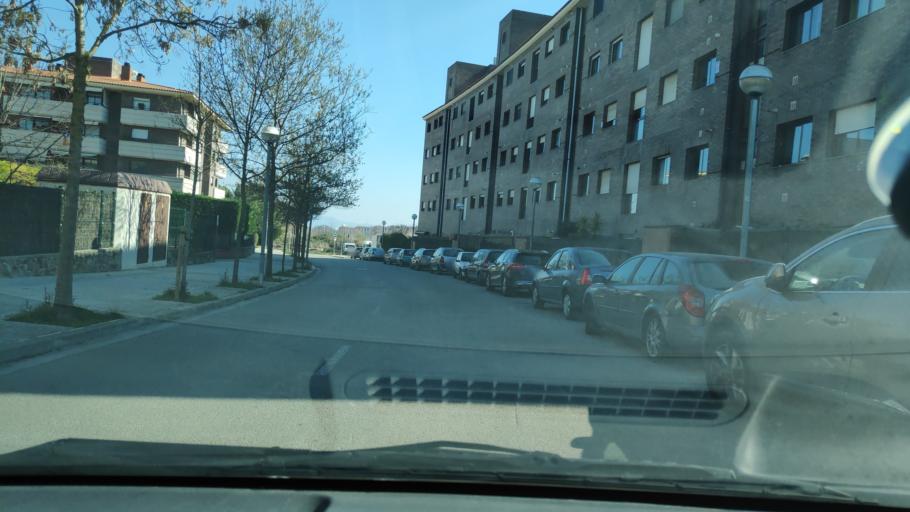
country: ES
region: Catalonia
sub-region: Provincia de Barcelona
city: Sant Quirze del Valles
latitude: 41.5543
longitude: 2.0744
